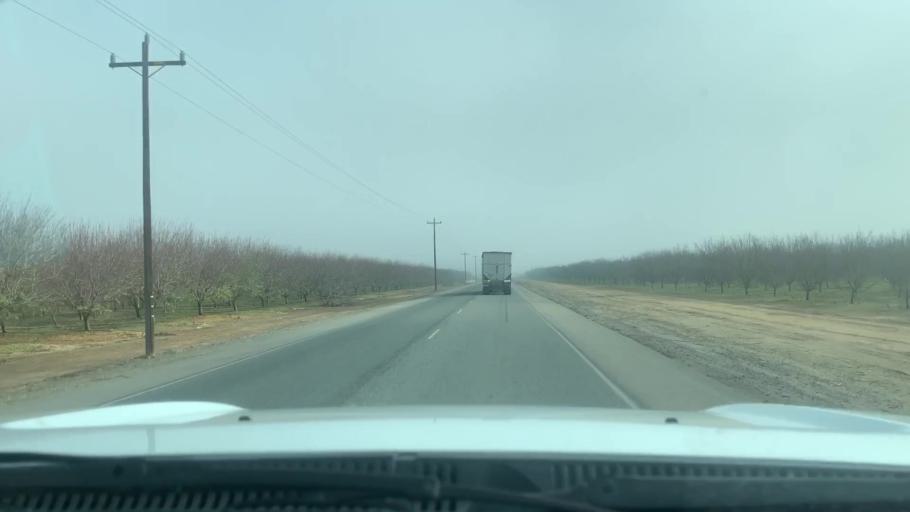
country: US
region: California
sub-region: Kern County
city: Buttonwillow
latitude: 35.5005
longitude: -119.4896
